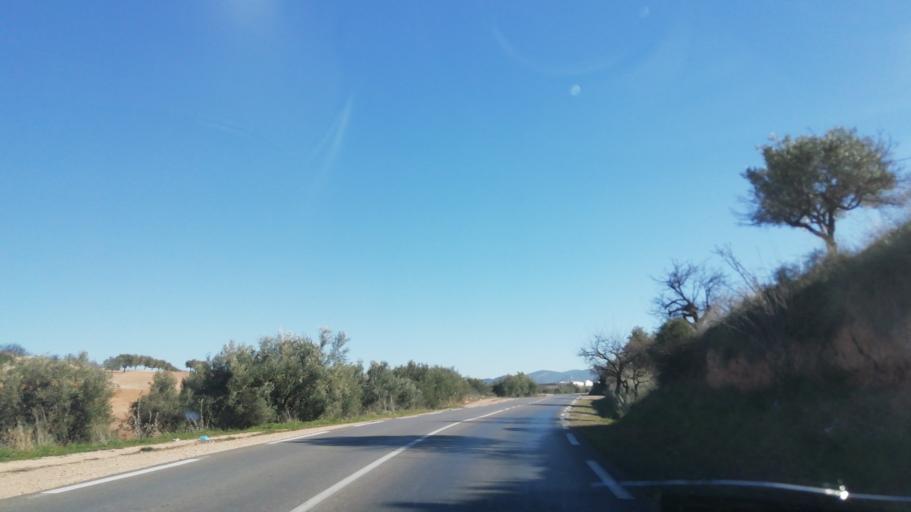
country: DZ
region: Tlemcen
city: Beni Mester
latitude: 34.8264
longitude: -1.5745
